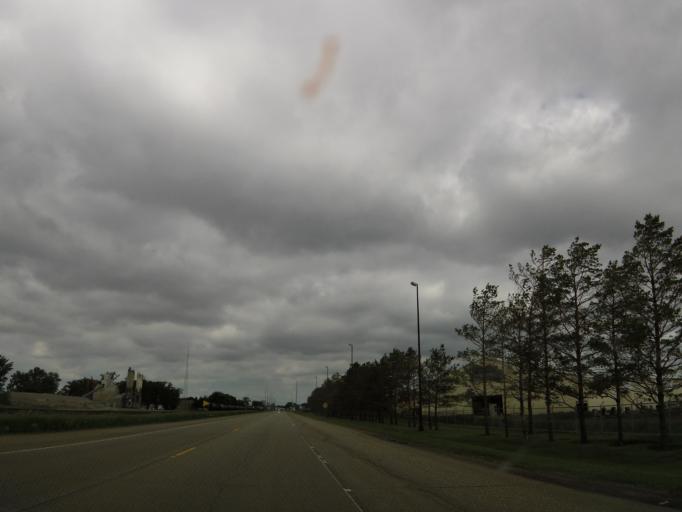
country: US
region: Minnesota
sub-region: Polk County
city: East Grand Forks
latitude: 47.9223
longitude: -97.0015
